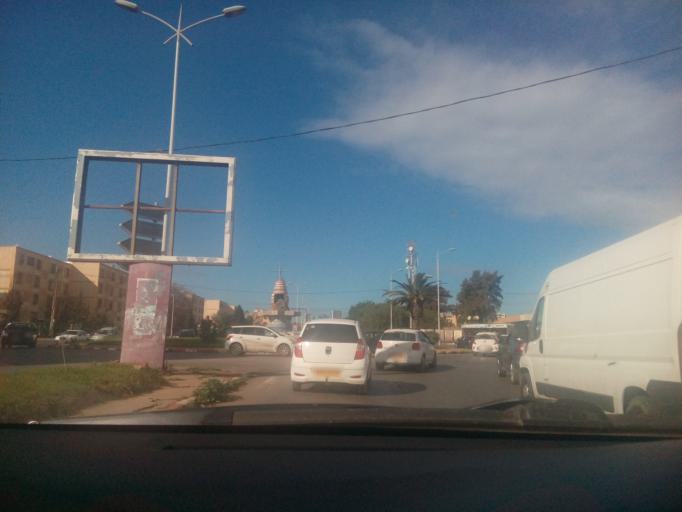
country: DZ
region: Oran
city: Oran
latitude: 35.6870
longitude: -0.6150
